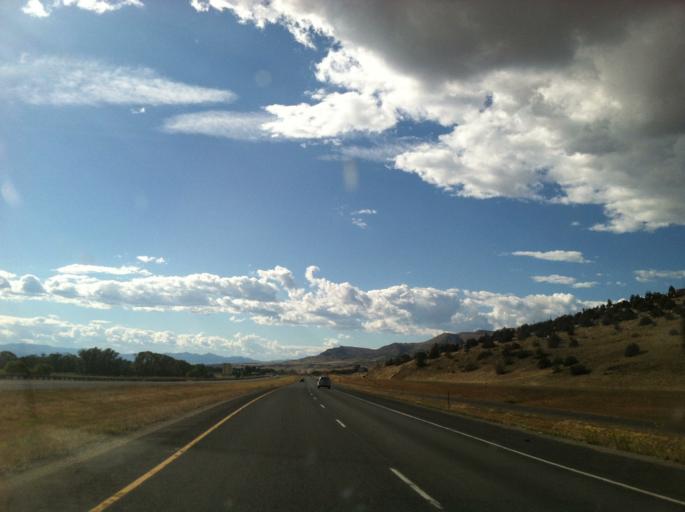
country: US
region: Montana
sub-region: Jefferson County
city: Whitehall
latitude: 45.8699
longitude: -111.9544
